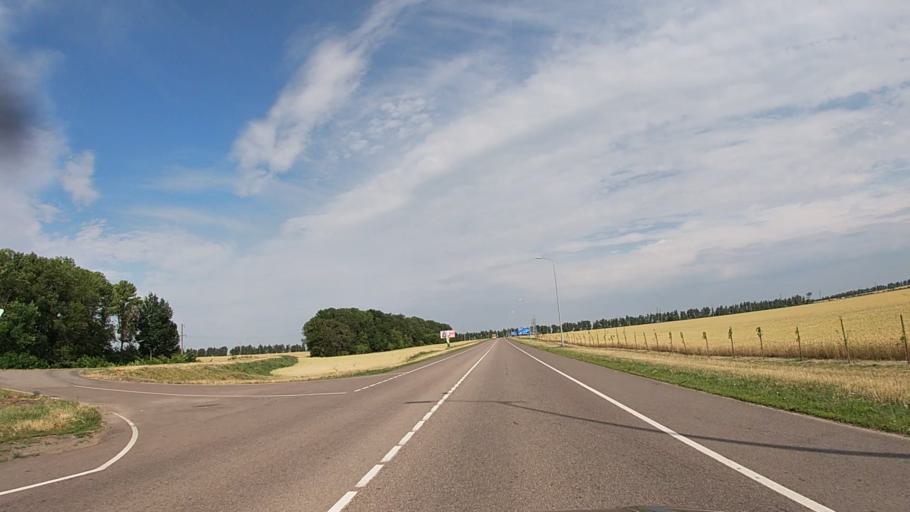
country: RU
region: Belgorod
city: Proletarskiy
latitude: 50.8283
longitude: 35.7743
